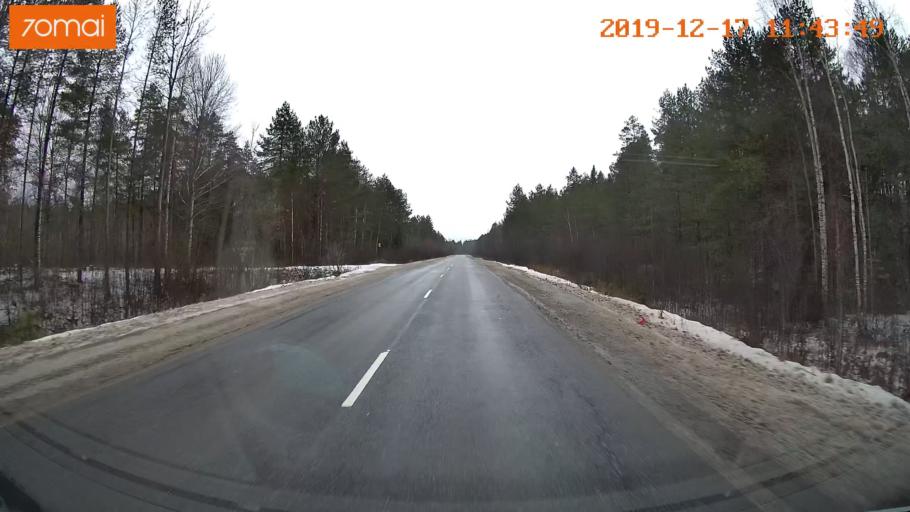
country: RU
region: Vladimir
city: Velikodvorskiy
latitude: 55.2709
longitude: 40.6682
